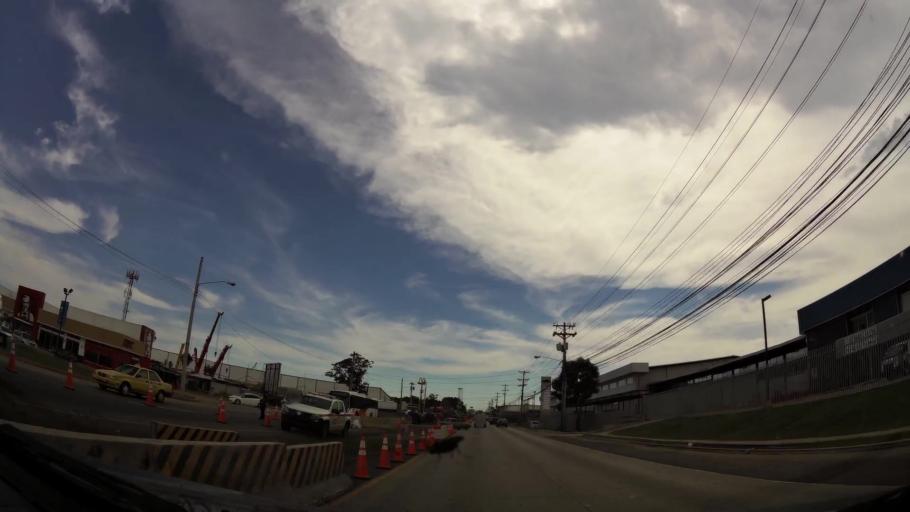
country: PA
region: Panama
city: Tocumen
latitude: 9.0775
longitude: -79.4010
